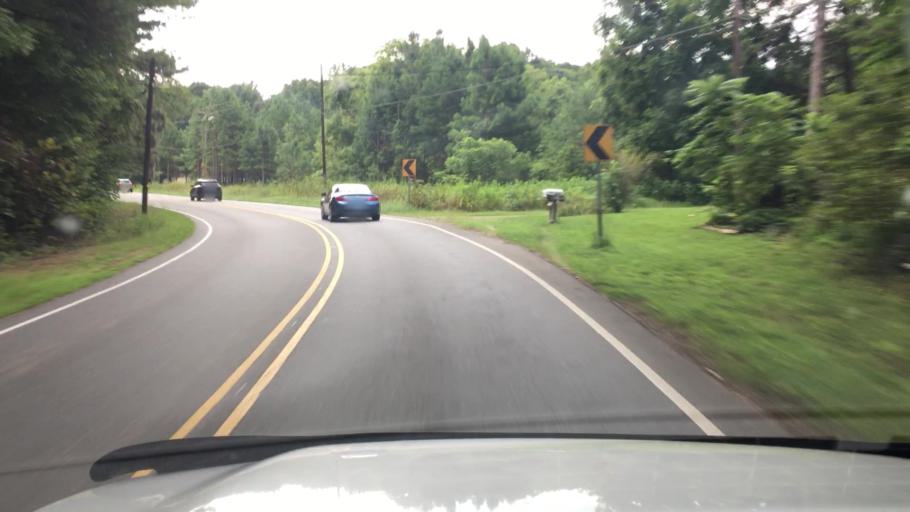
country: US
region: North Carolina
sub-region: Mecklenburg County
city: Huntersville
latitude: 35.3605
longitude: -80.8972
